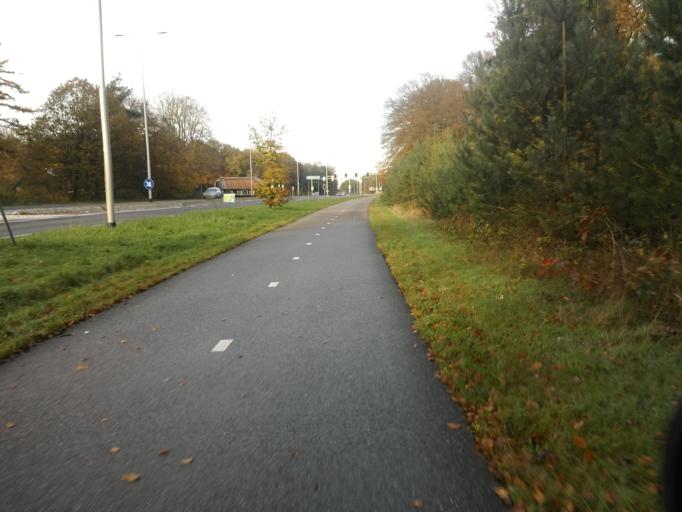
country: NL
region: Utrecht
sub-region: Gemeente Utrechtse Heuvelrug
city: Maarn
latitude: 52.0902
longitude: 5.3618
